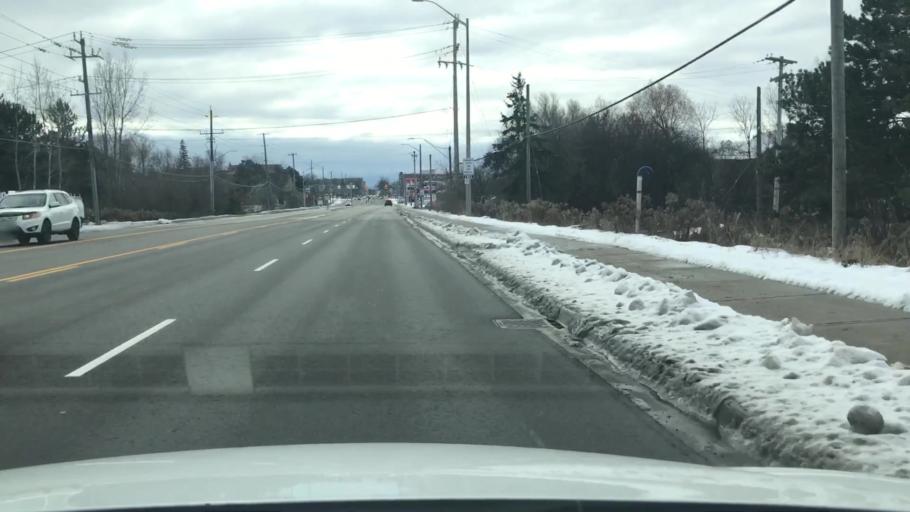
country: CA
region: Ontario
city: Newmarket
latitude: 44.0110
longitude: -79.4703
